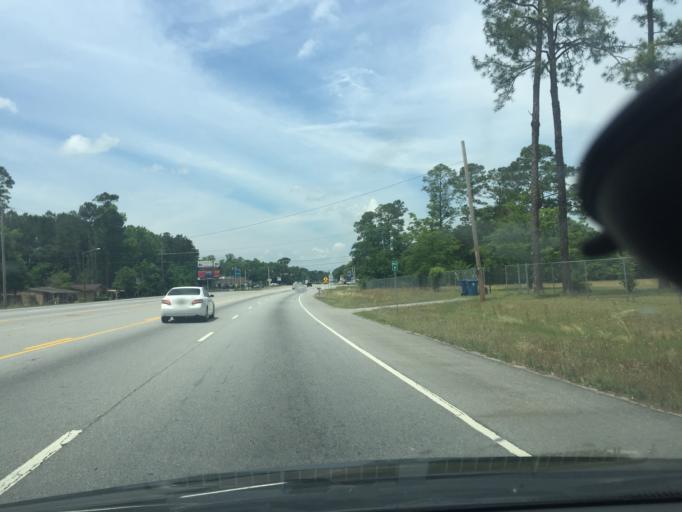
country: US
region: Georgia
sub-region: Chatham County
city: Bloomingdale
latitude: 32.1441
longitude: -81.3348
